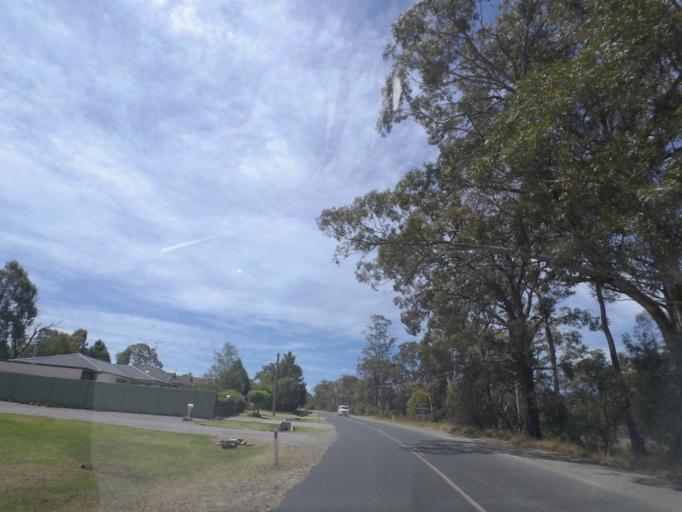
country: AU
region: New South Wales
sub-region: Wingecarribee
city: Colo Vale
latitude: -34.3737
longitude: 150.5413
